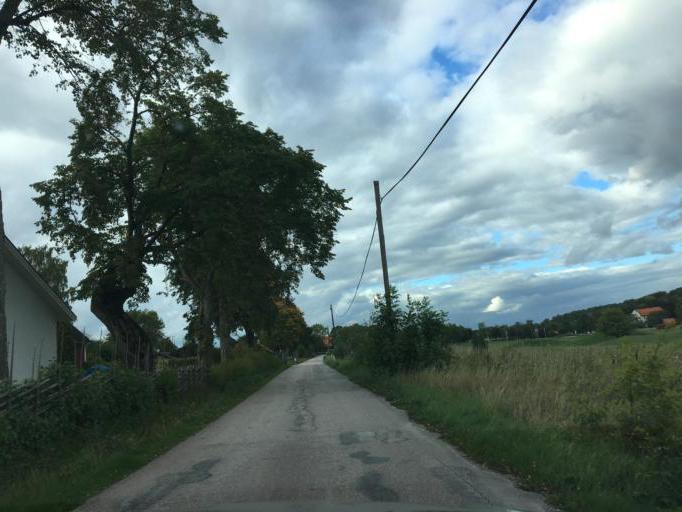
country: SE
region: Vaestmanland
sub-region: Vasteras
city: Tillberga
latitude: 59.5346
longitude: 16.7536
